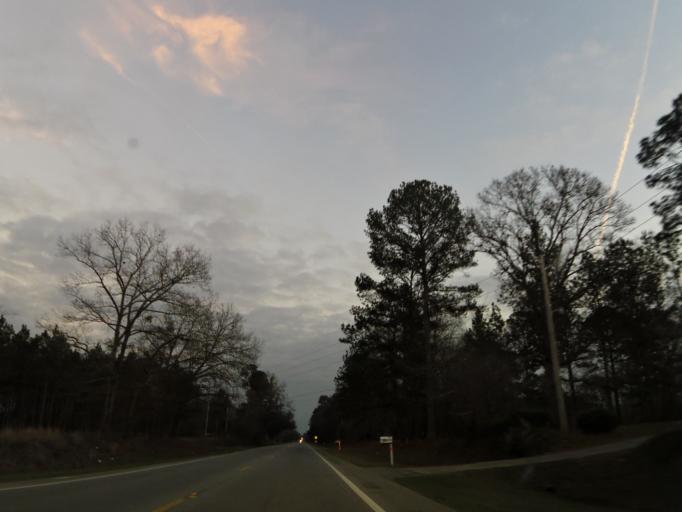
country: US
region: Georgia
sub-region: Dougherty County
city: Putney
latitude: 31.4724
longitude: -84.0092
